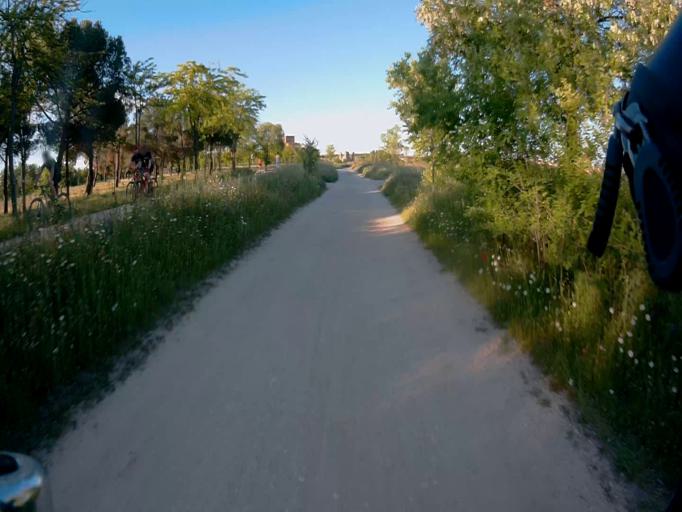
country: ES
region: Madrid
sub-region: Provincia de Madrid
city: Fuenlabrada
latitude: 40.3153
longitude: -3.7991
